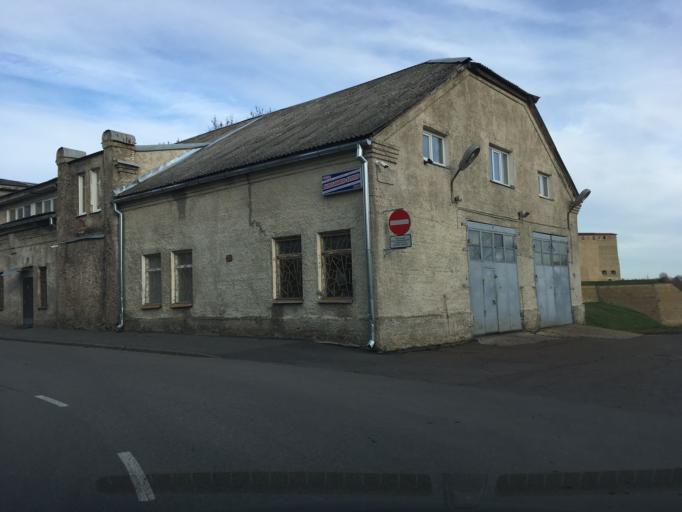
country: EE
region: Ida-Virumaa
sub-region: Narva linn
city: Narva
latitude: 59.3740
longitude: 28.1976
